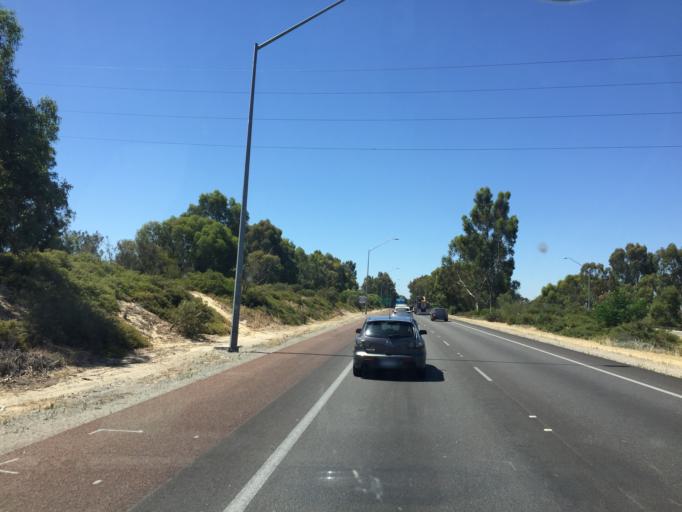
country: AU
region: Western Australia
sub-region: Gosnells
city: Kenwick
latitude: -32.0211
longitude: 115.9719
